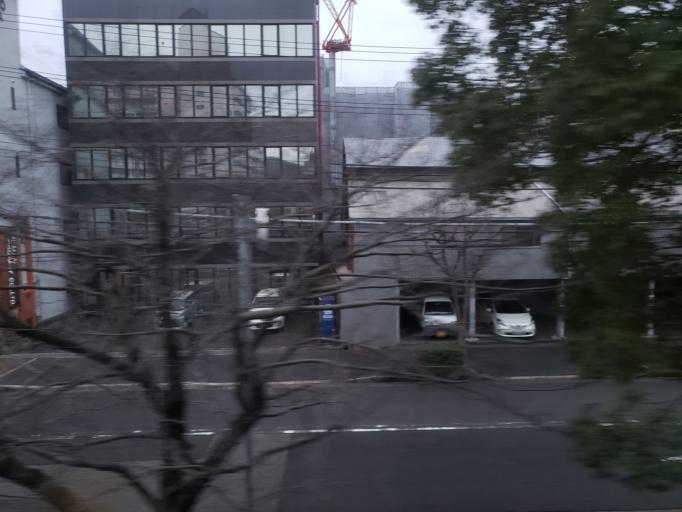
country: JP
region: Hyogo
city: Kobe
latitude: 34.6555
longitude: 135.1416
